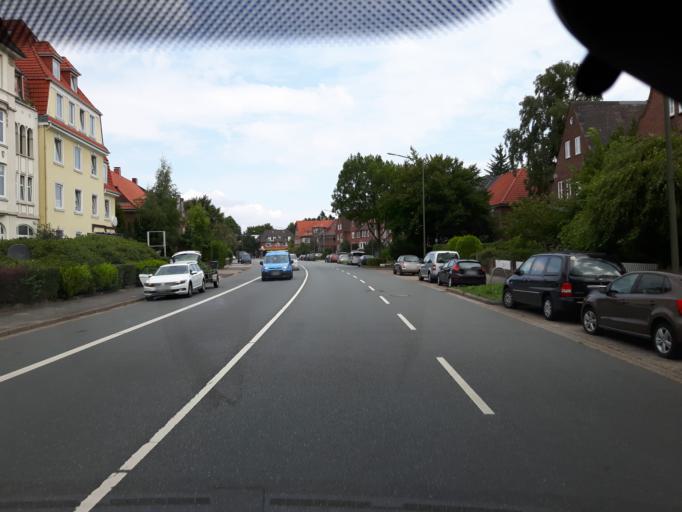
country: DE
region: Schleswig-Holstein
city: Flensburg
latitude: 54.7892
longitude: 9.4464
